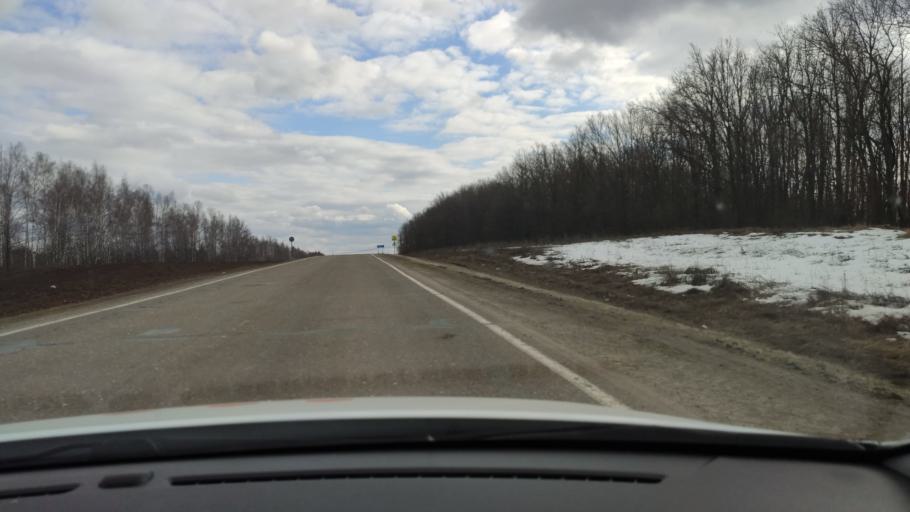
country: RU
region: Tatarstan
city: Vysokaya Gora
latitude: 56.0788
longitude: 49.1875
